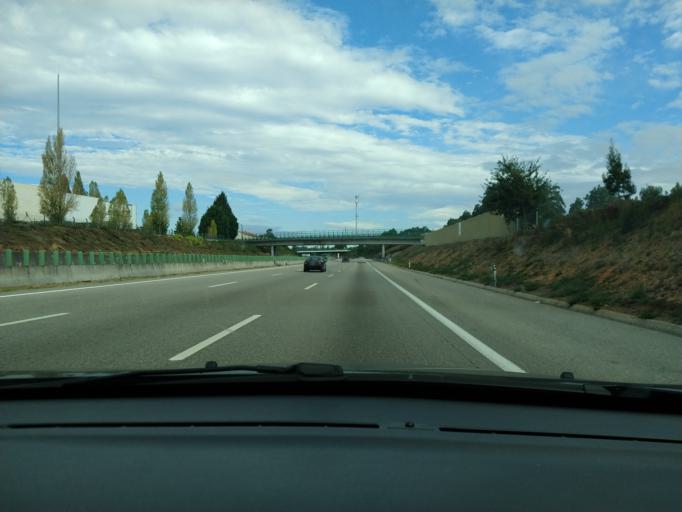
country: PT
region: Aveiro
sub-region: Ovar
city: Valega
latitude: 40.8769
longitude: -8.5604
